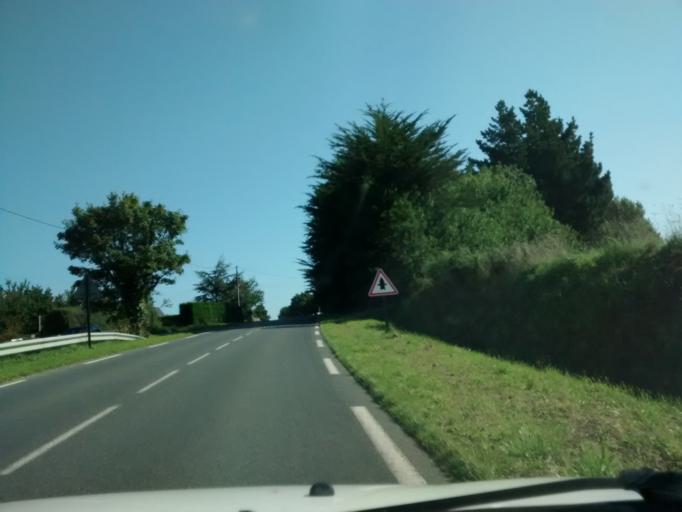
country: FR
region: Brittany
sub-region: Departement des Cotes-d'Armor
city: Tredarzec
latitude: 48.8144
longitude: -3.1929
